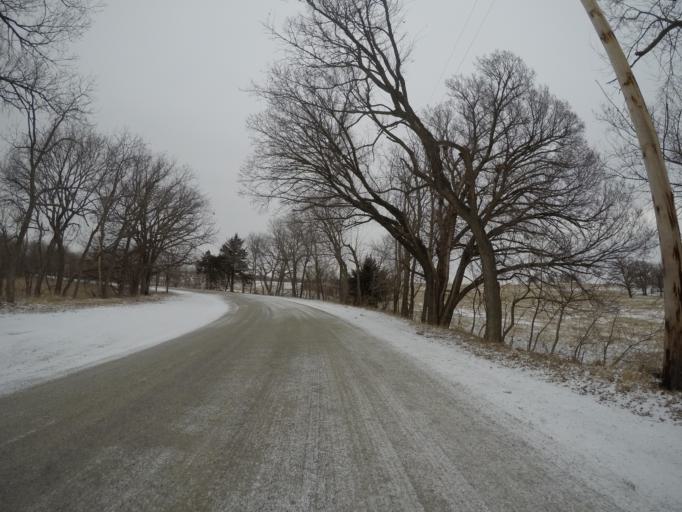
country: US
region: Kansas
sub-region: Wabaunsee County
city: Alma
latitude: 38.8629
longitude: -96.1793
